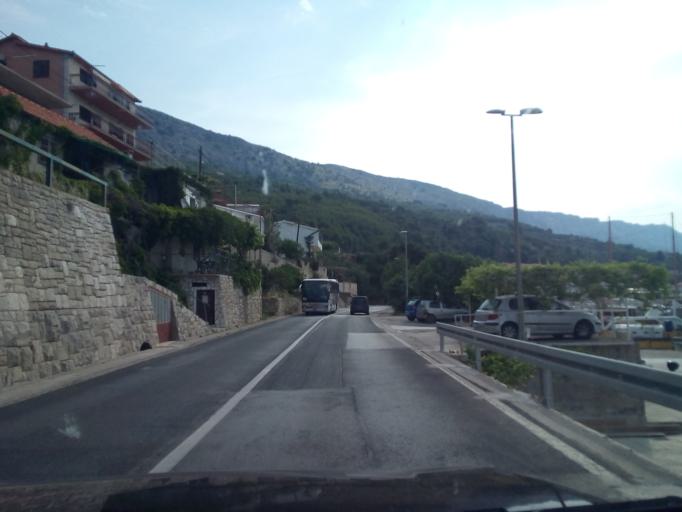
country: HR
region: Splitsko-Dalmatinska
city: Srinjine
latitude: 43.4643
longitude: 16.5830
